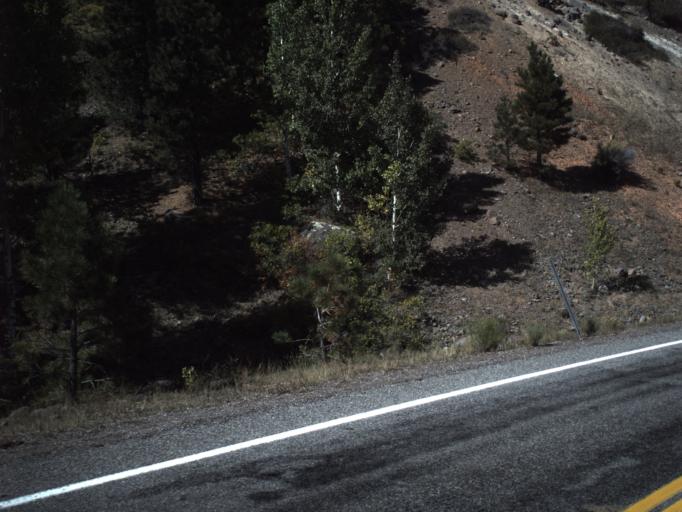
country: US
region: Utah
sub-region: Wayne County
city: Loa
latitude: 38.1500
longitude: -111.3326
